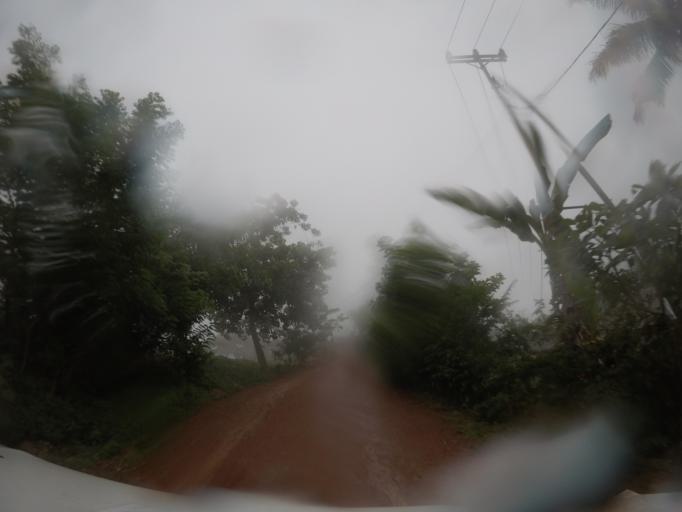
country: TL
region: Baucau
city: Venilale
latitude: -8.6360
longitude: 126.4208
